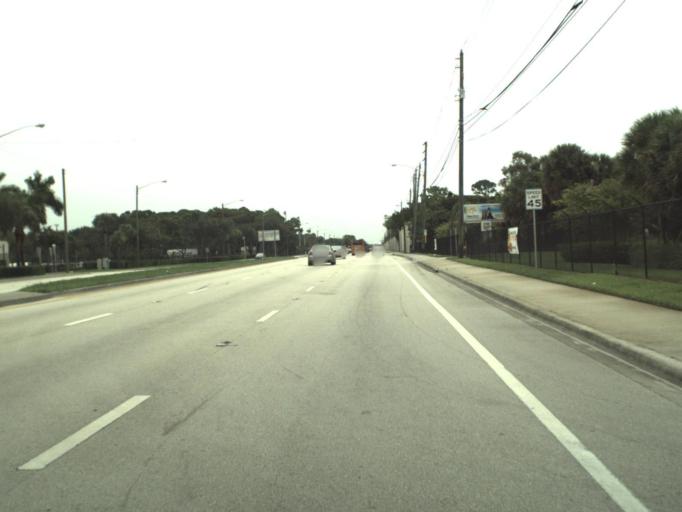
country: US
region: Florida
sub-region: Palm Beach County
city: Schall Circle
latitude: 26.7225
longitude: -80.1104
